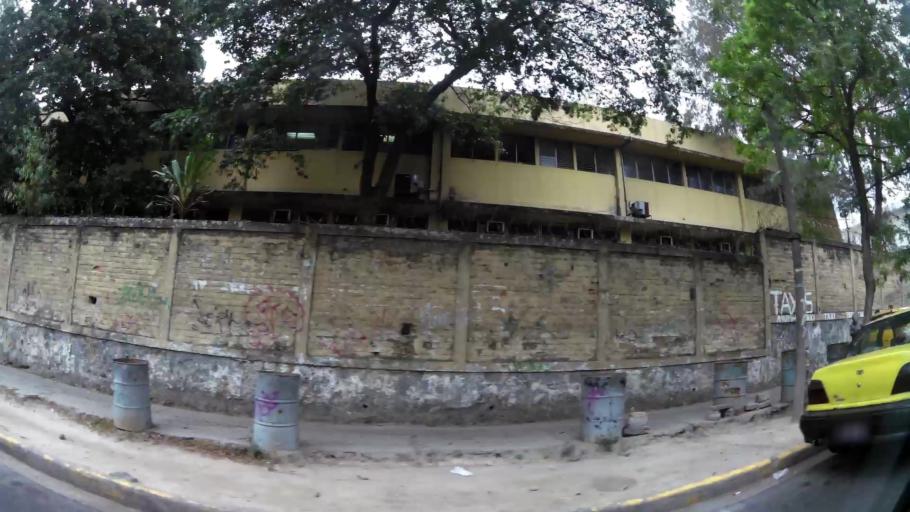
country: SV
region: San Salvador
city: San Salvador
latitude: 13.7014
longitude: -89.2053
